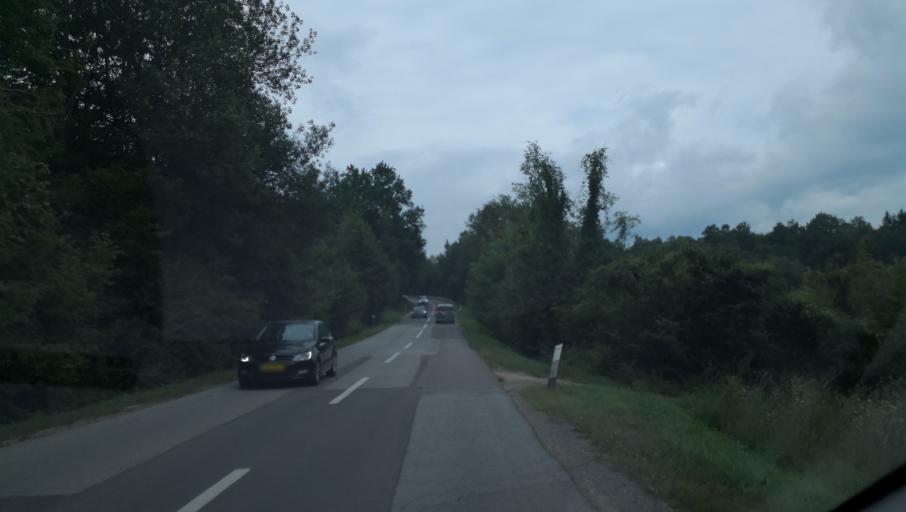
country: HR
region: Karlovacka
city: Ozalj
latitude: 45.5200
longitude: 15.3939
